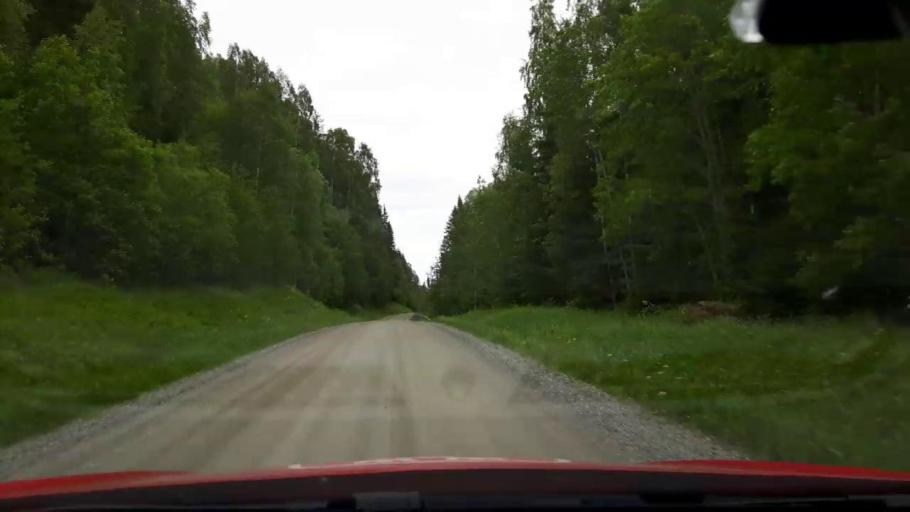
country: SE
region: Jaemtland
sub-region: Ragunda Kommun
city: Hammarstrand
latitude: 63.1871
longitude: 16.1439
